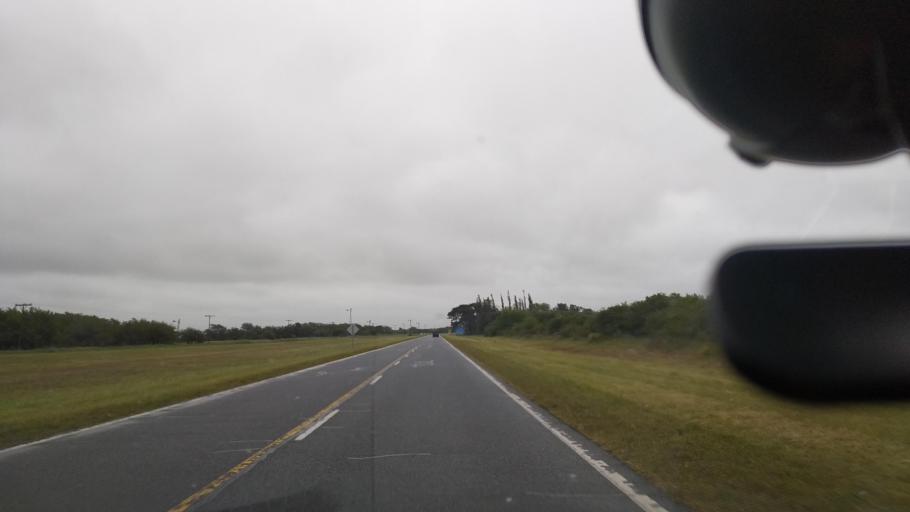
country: AR
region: Buenos Aires
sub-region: Partido de Castelli
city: Castelli
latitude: -35.9530
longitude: -57.4484
